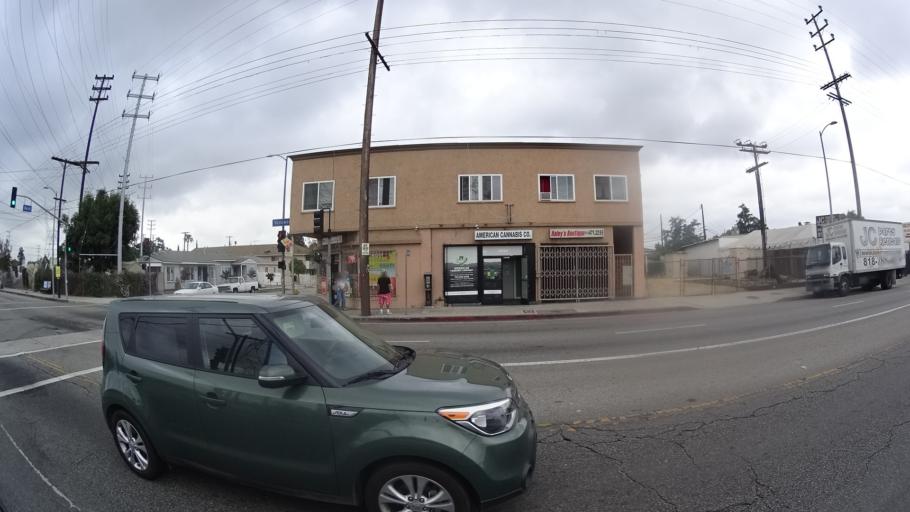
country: US
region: California
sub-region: Los Angeles County
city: North Hollywood
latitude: 34.1941
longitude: -118.3835
